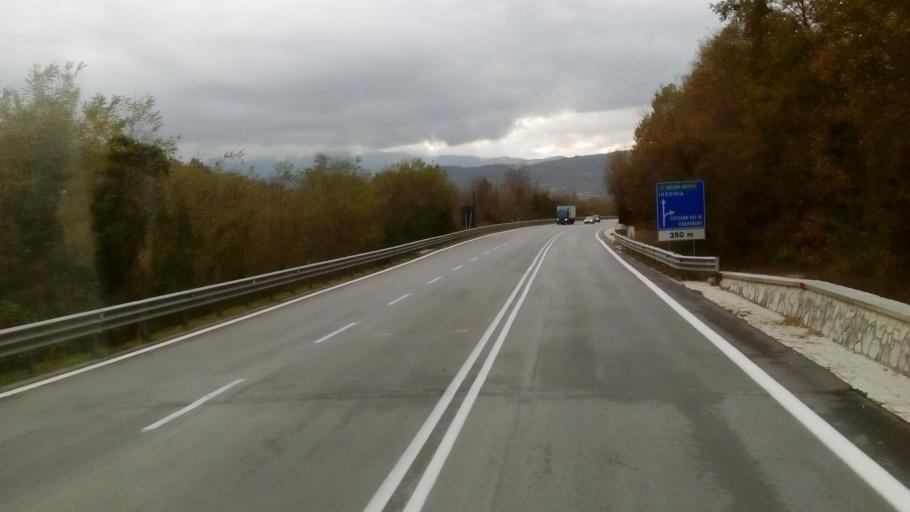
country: IT
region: Molise
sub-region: Provincia di Isernia
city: Sessano del Molise
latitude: 41.6486
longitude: 14.3316
